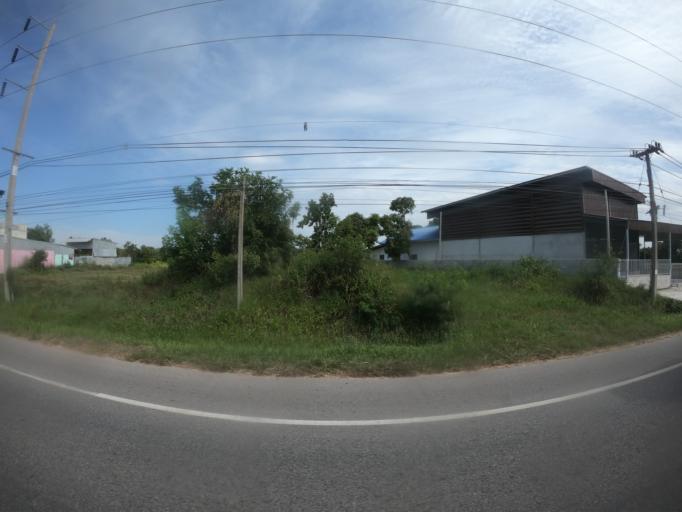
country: TH
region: Maha Sarakham
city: Chiang Yuen
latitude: 16.4243
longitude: 103.0700
